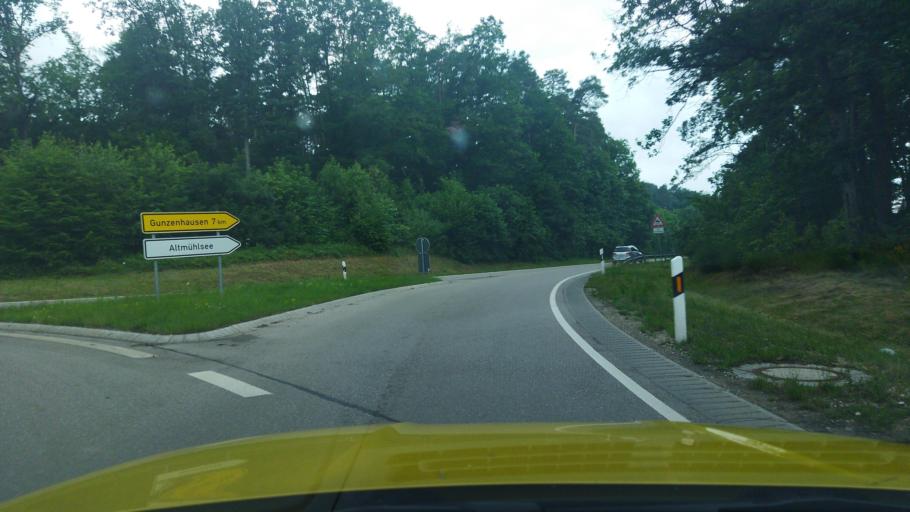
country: DE
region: Bavaria
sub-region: Regierungsbezirk Mittelfranken
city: Pfofeld
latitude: 49.1176
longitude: 10.8473
